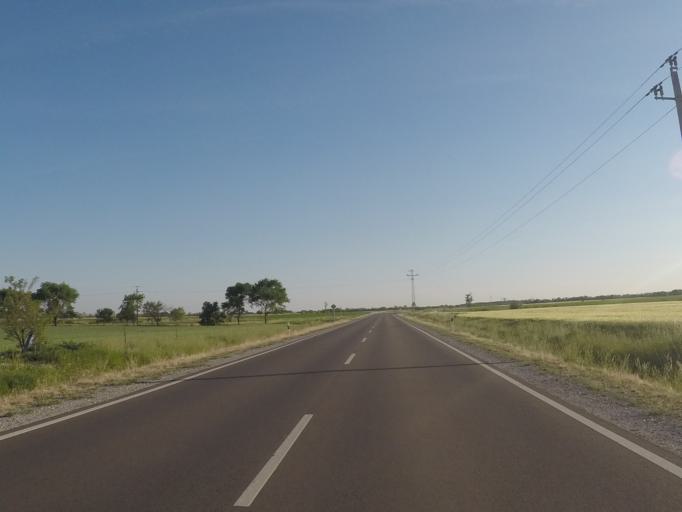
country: HU
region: Heves
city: Besenyotelek
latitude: 47.6857
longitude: 20.3879
